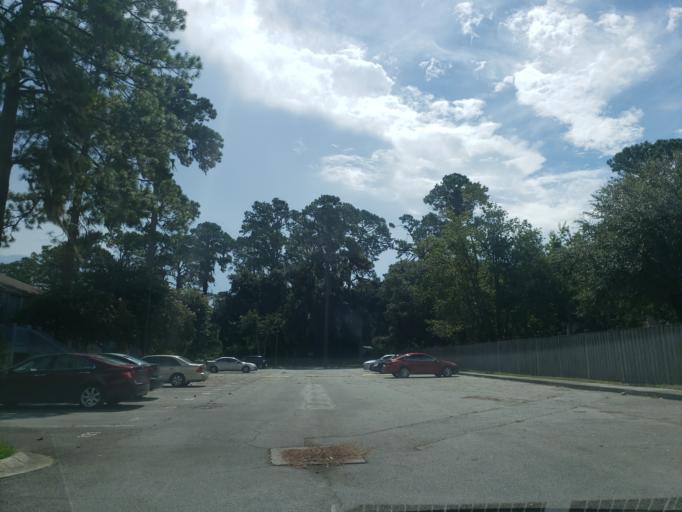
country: US
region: Georgia
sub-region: Chatham County
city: Wilmington Island
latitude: 32.0299
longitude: -80.9601
